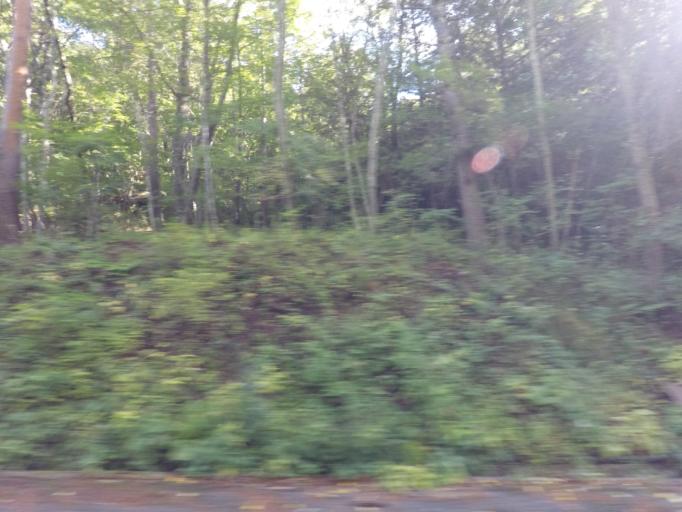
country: JP
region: Nagano
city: Tatsuno
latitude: 35.9651
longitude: 137.7745
